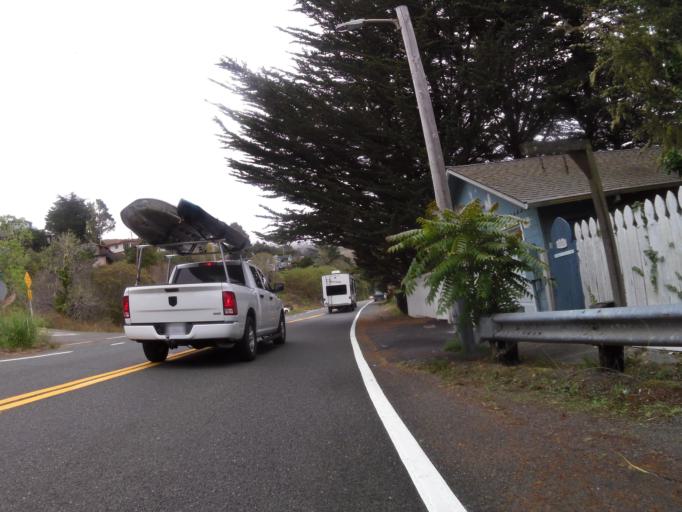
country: US
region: California
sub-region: Sonoma County
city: Monte Rio
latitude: 38.4508
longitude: -123.1204
